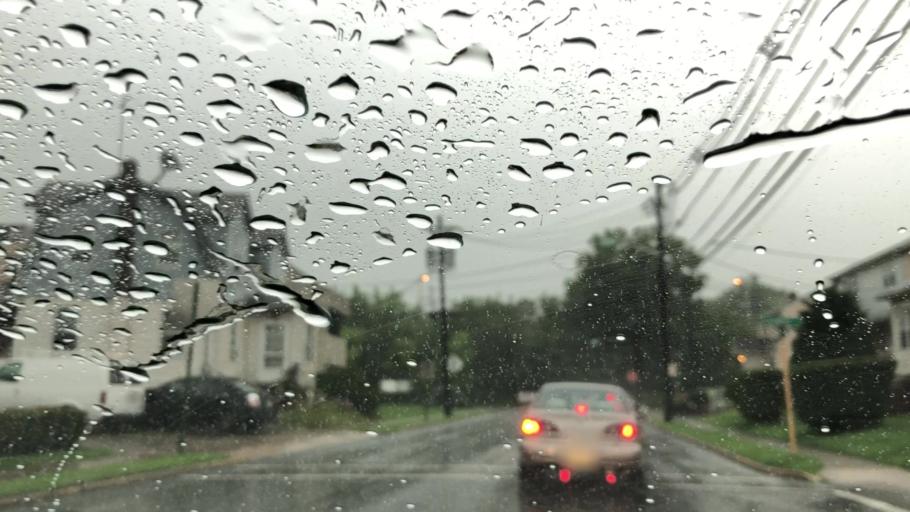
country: US
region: New Jersey
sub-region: Bergen County
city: Elmwood Park
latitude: 40.9054
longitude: -74.1129
